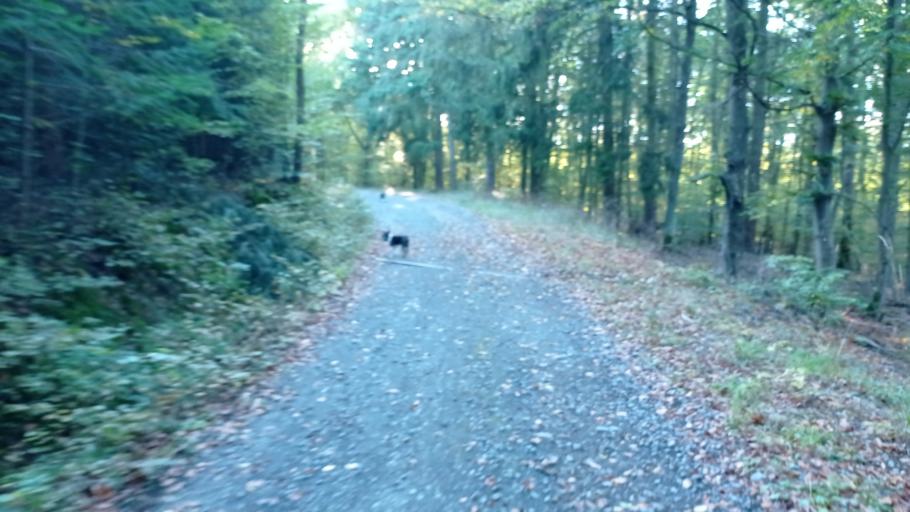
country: CZ
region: Central Bohemia
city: Chynava
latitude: 50.0638
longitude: 14.0624
